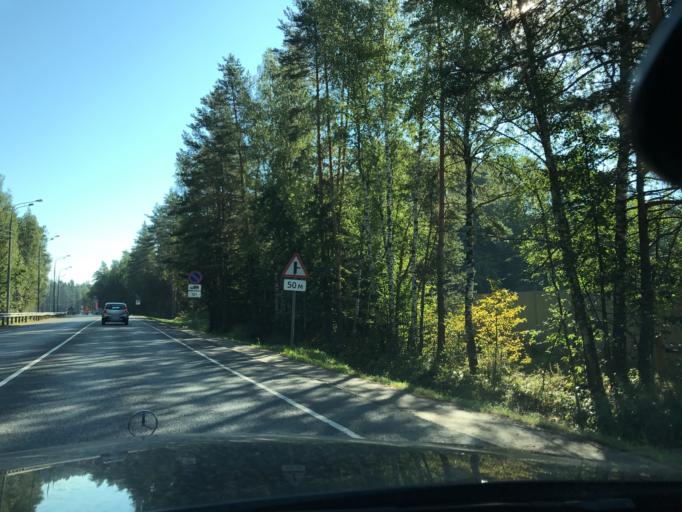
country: RU
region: Moskovskaya
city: Chernogolovka
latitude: 55.9829
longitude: 38.3322
